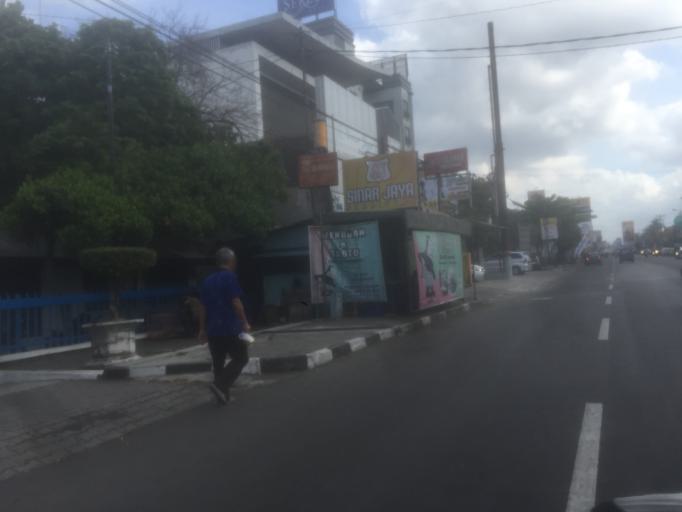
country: ID
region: Daerah Istimewa Yogyakarta
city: Yogyakarta
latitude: -7.7696
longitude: 110.3614
